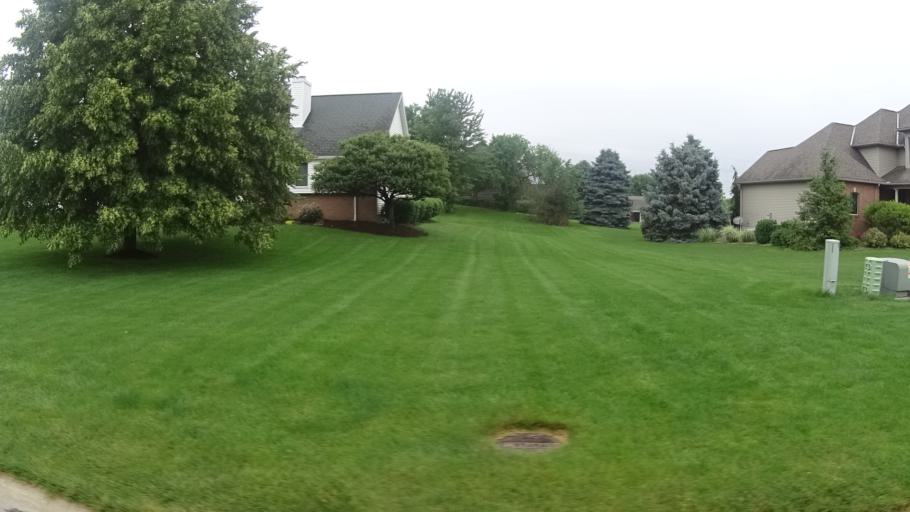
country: US
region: Ohio
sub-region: Erie County
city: Huron
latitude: 41.3581
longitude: -82.5739
